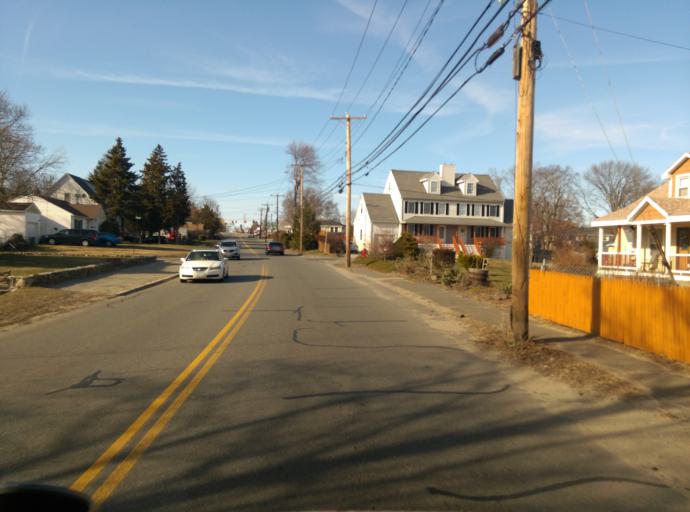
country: US
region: Massachusetts
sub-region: Essex County
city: North Andover
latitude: 42.7242
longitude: -71.1406
